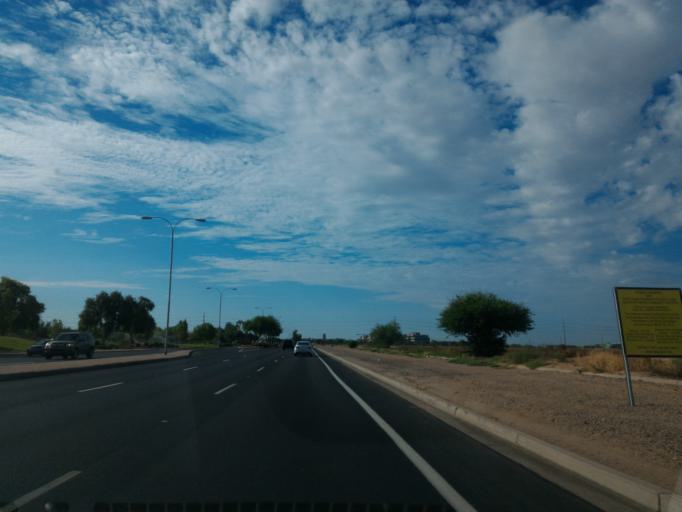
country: US
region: Arizona
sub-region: Maricopa County
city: Chandler
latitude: 33.2756
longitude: -111.8893
